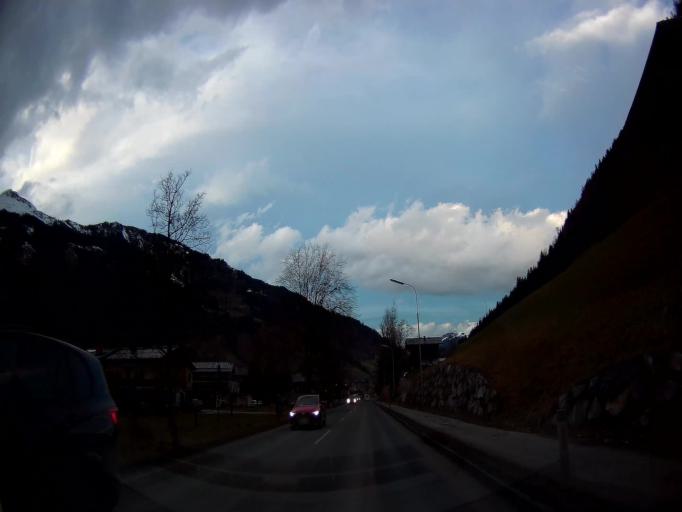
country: AT
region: Salzburg
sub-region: Politischer Bezirk Sankt Johann im Pongau
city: Bad Hofgastein
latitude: 47.1825
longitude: 13.1015
